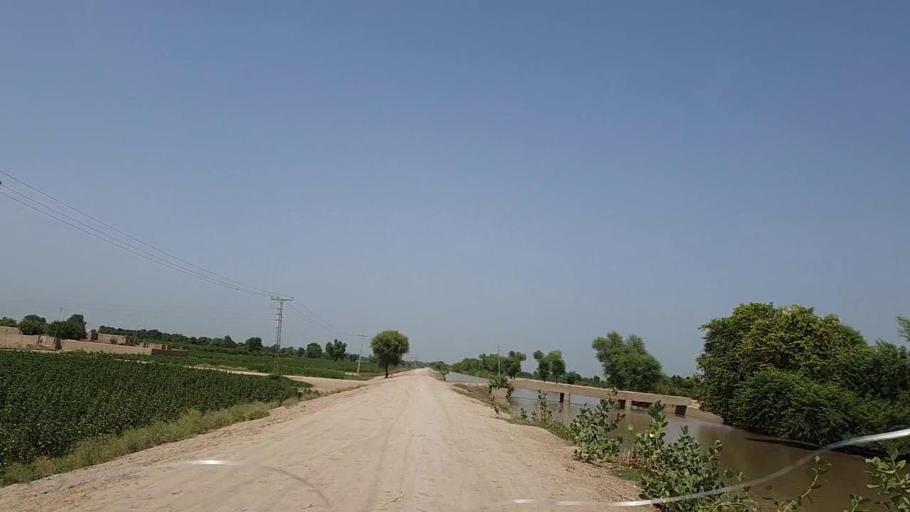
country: PK
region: Sindh
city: Kandiaro
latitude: 27.0409
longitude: 68.1548
